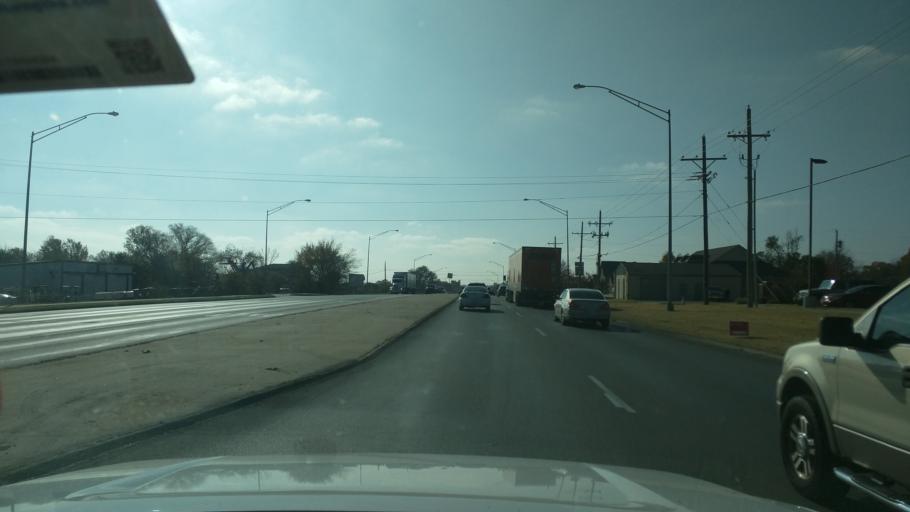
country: US
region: Oklahoma
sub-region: Washington County
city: Bartlesville
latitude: 36.7279
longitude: -95.9352
